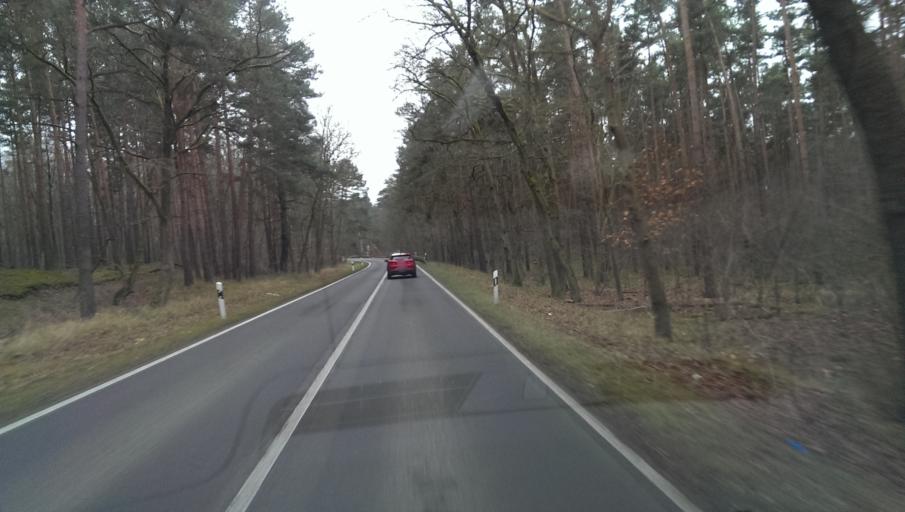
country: DE
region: Brandenburg
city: Grossbeeren
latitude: 52.3290
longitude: 13.3002
